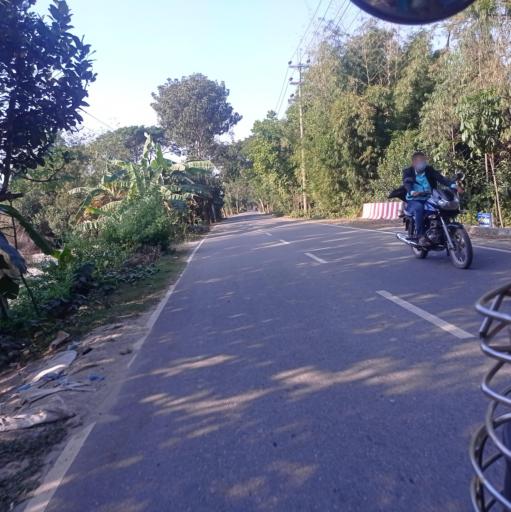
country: BD
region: Dhaka
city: Bajitpur
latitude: 24.1450
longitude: 90.8153
